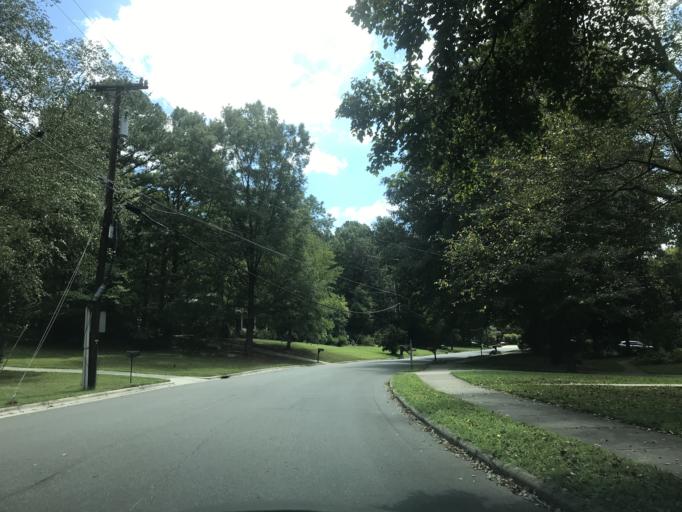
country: US
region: North Carolina
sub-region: Orange County
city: Chapel Hill
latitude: 35.9299
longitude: -79.0201
